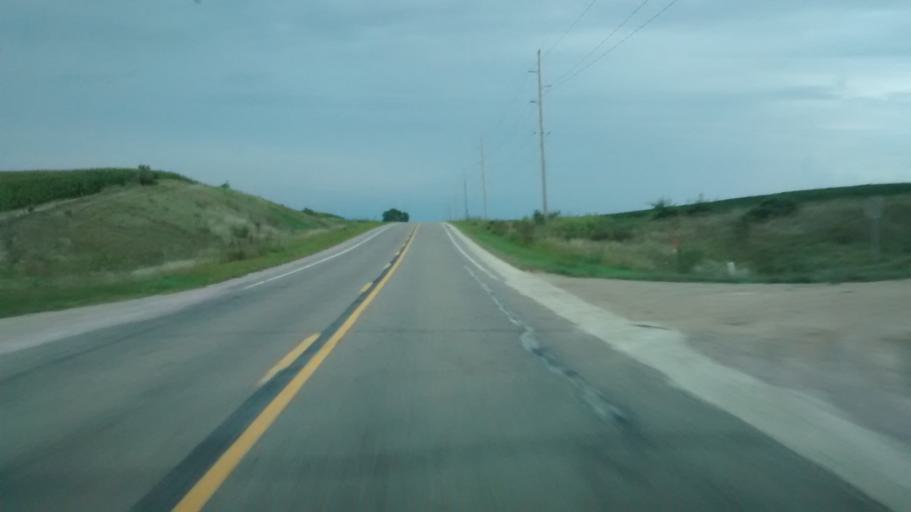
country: US
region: Iowa
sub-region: Woodbury County
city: Moville
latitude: 42.5184
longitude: -96.0481
